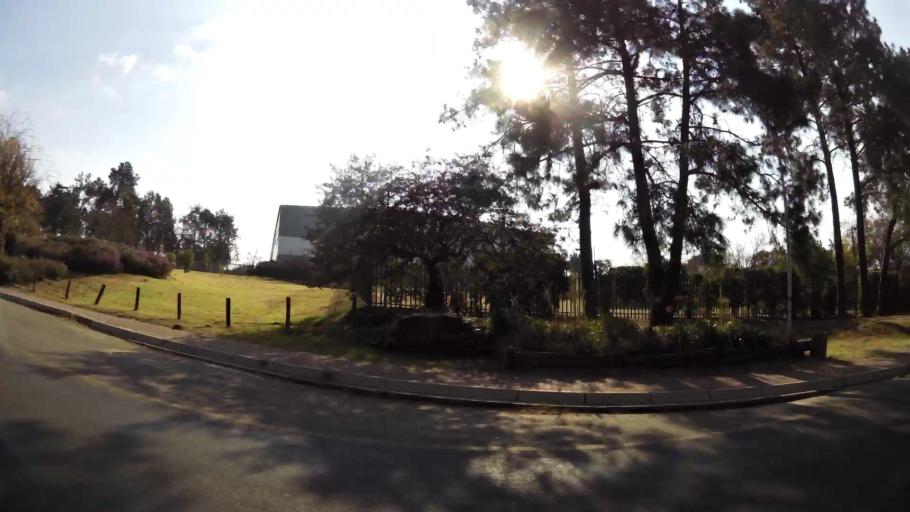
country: ZA
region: Gauteng
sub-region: City of Johannesburg Metropolitan Municipality
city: Modderfontein
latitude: -26.1071
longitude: 28.1485
